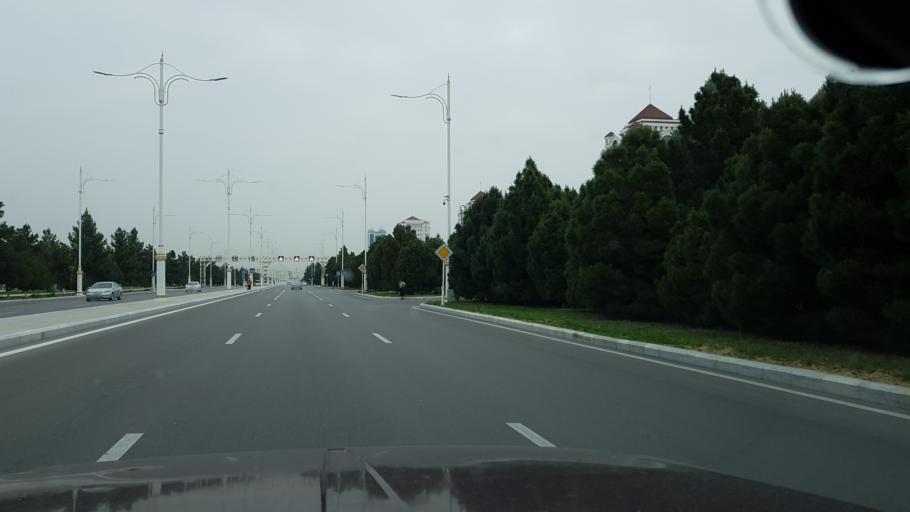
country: TM
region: Ahal
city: Ashgabat
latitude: 37.8839
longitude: 58.3875
